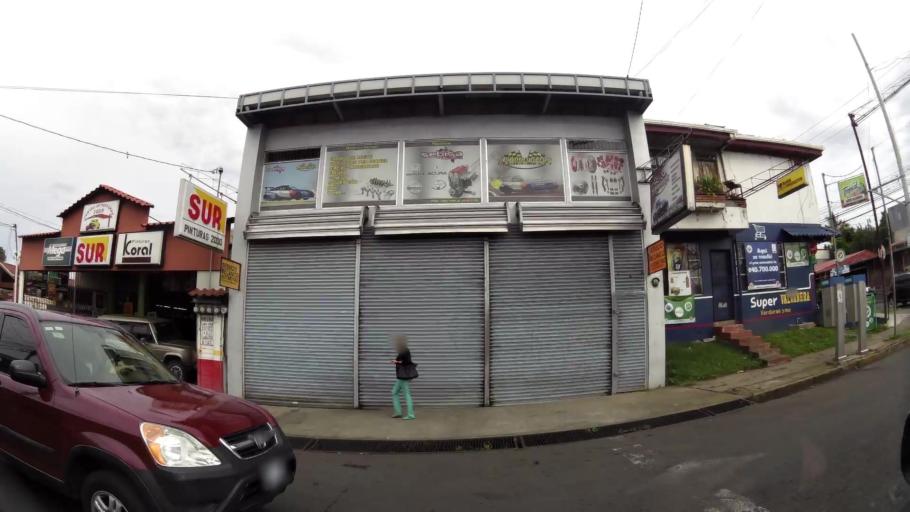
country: CR
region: San Jose
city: San Juan
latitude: 9.9624
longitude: -84.0829
